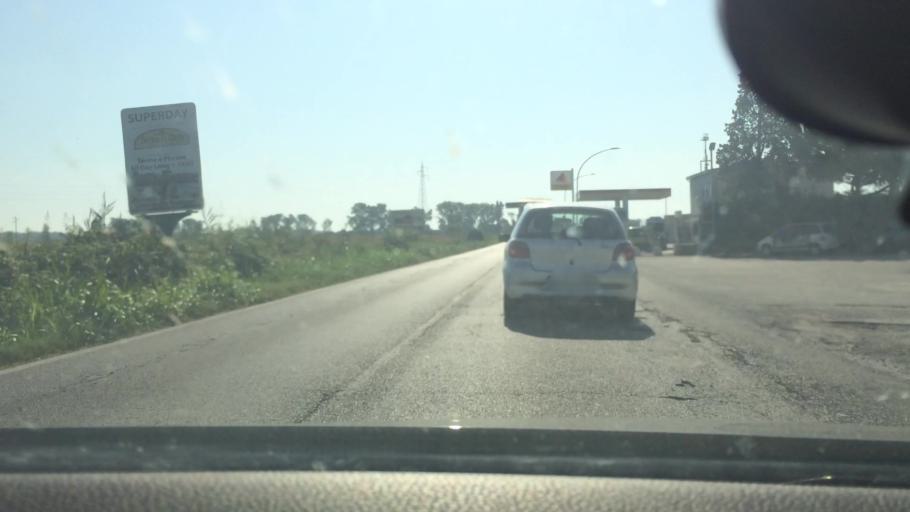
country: IT
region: Emilia-Romagna
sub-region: Provincia di Ferrara
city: Comacchio
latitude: 44.6918
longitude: 12.1976
